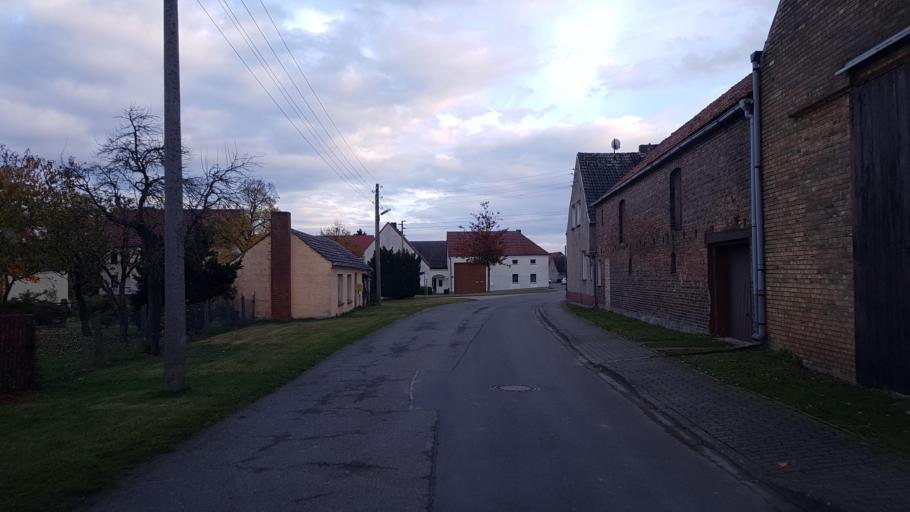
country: DE
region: Saxony-Anhalt
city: Seyda
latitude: 51.9246
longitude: 12.8882
